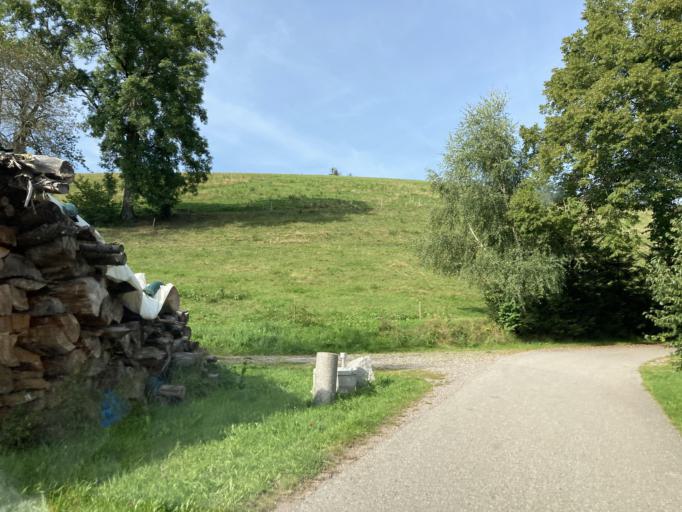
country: DE
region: Baden-Wuerttemberg
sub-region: Freiburg Region
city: Sankt Georgen im Schwarzwald
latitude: 48.1184
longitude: 8.3156
